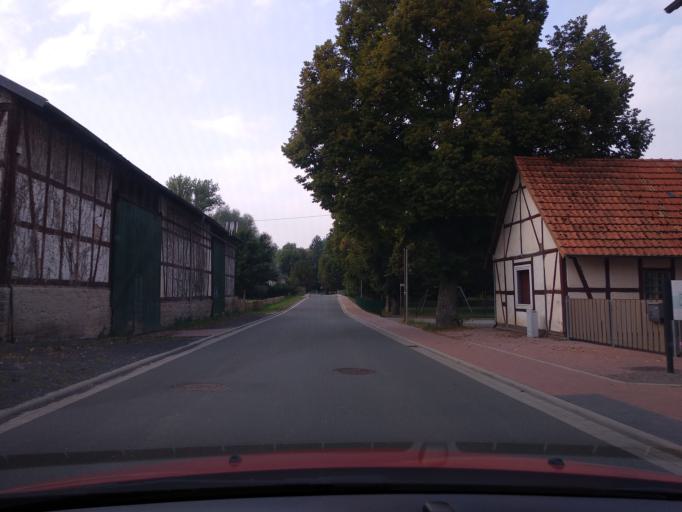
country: DE
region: Hesse
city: Liebenau
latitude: 51.4967
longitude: 9.2819
